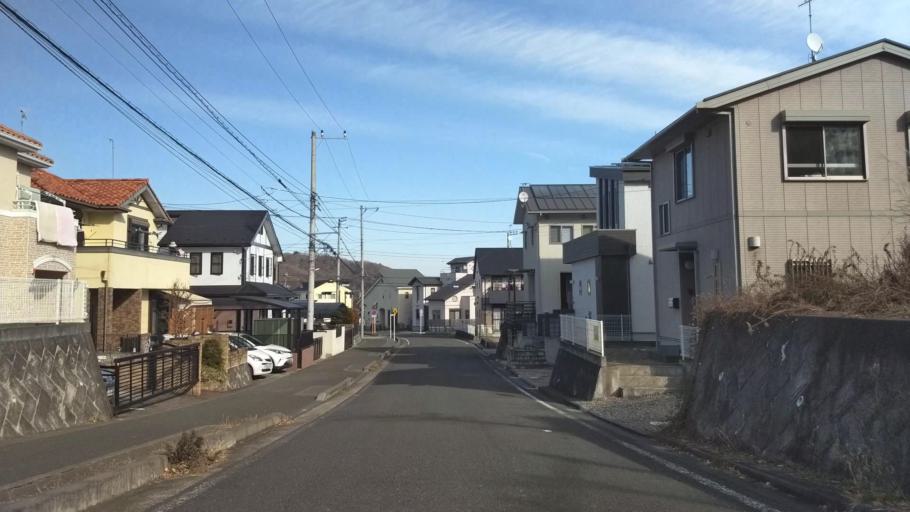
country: JP
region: Kanagawa
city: Hadano
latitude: 35.3584
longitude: 139.2289
